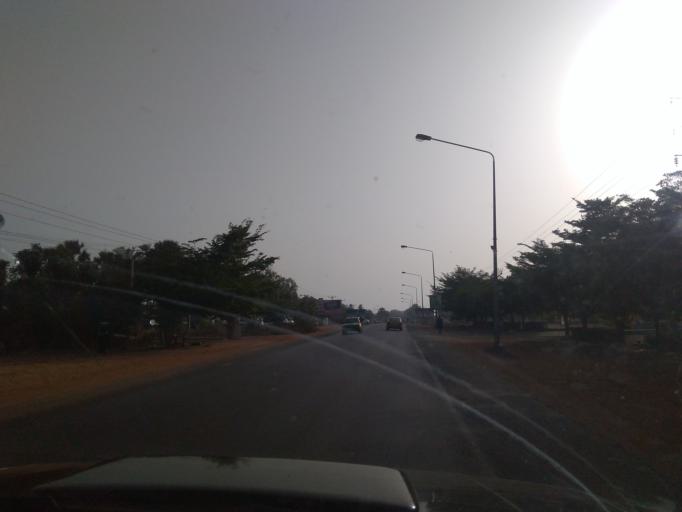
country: GM
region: Banjul
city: Bakau
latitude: 13.4571
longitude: -16.7010
